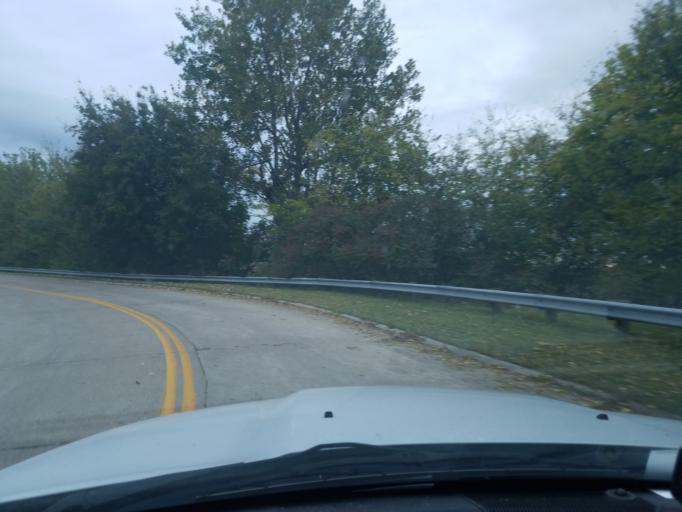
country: US
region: Indiana
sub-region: Vanderburgh County
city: Evansville
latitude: 37.9157
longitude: -87.5494
